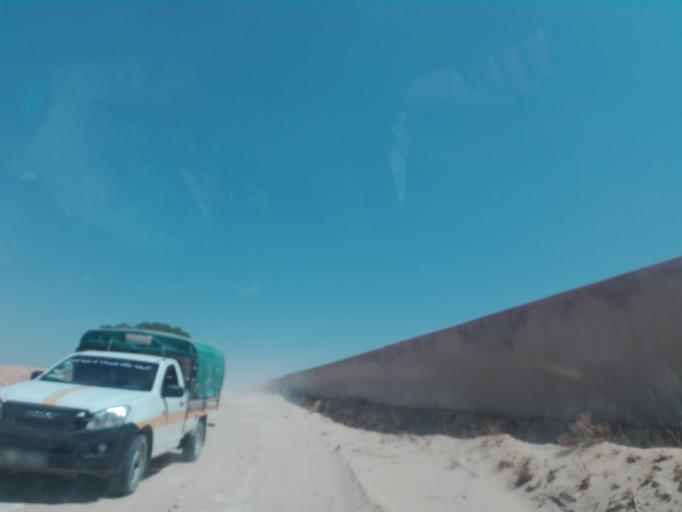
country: TN
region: Safaqis
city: Skhira
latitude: 34.4142
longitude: 9.9345
